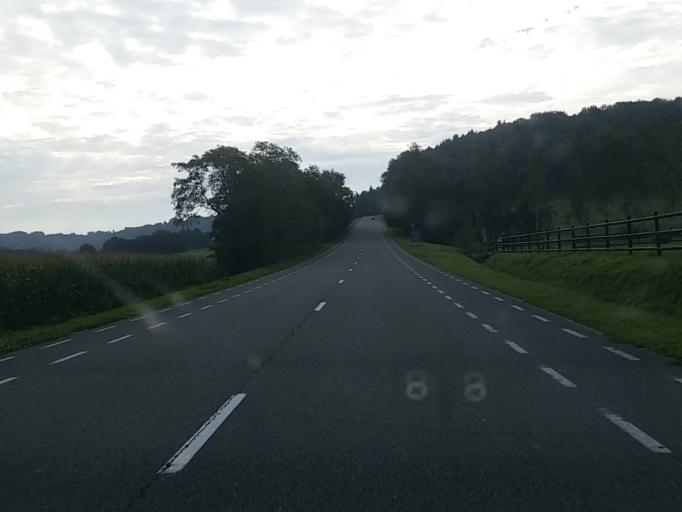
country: BE
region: Wallonia
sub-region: Province du Luxembourg
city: Florenville
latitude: 49.7143
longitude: 5.2537
